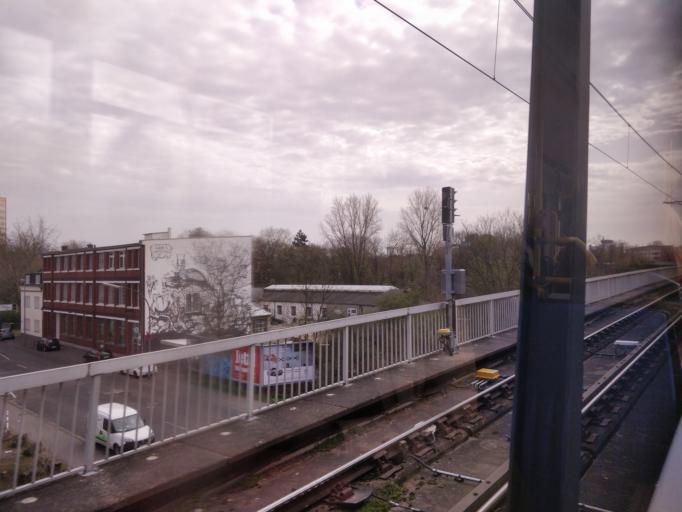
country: DE
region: North Rhine-Westphalia
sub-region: Regierungsbezirk Koln
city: Nippes
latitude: 50.9724
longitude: 6.9546
